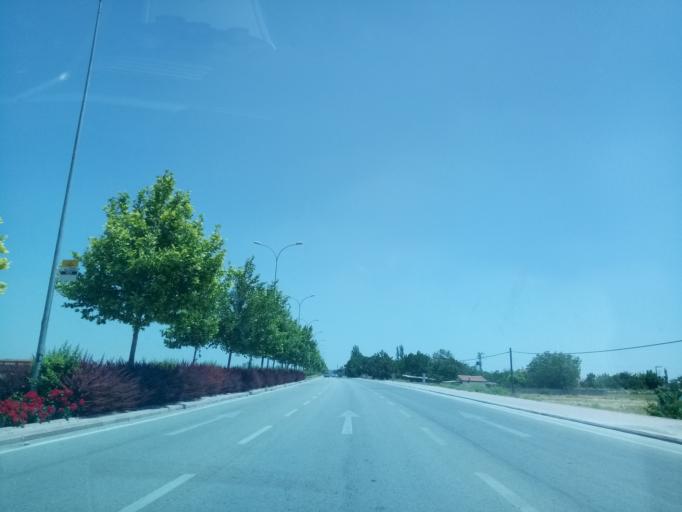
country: TR
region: Konya
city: Meram
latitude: 37.8149
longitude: 32.4472
